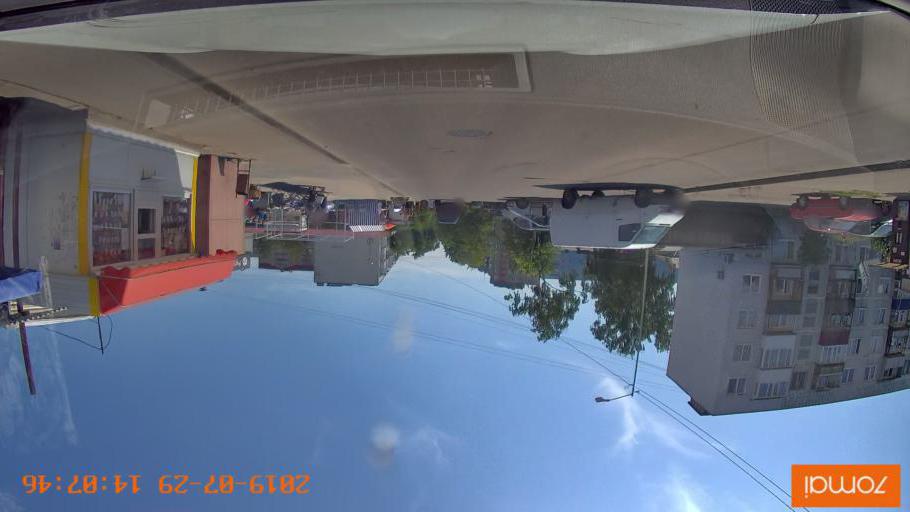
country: RU
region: Kaliningrad
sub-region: Gorod Kaliningrad
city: Baltiysk
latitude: 54.6583
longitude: 19.9098
